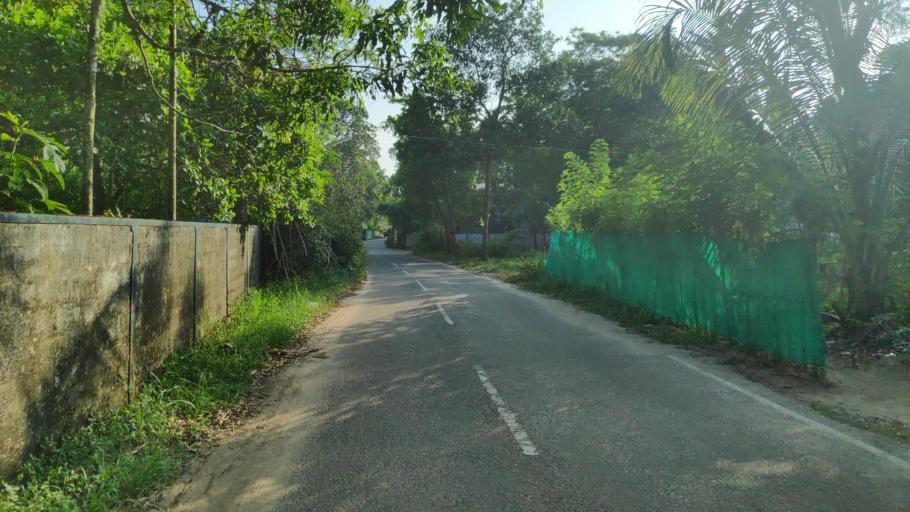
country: IN
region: Kerala
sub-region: Alappuzha
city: Alleppey
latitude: 9.5813
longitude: 76.3408
